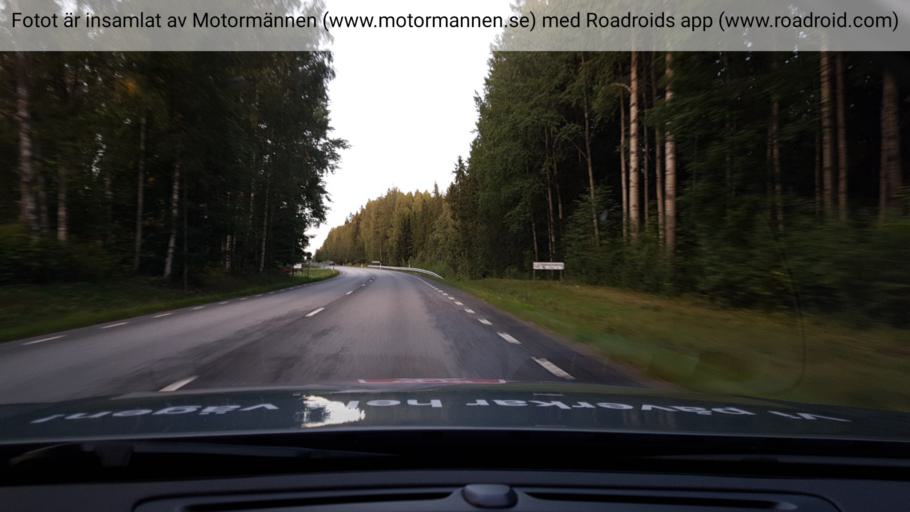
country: SE
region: OErebro
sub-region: Hallefors Kommun
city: Haellefors
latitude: 59.7899
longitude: 14.5395
